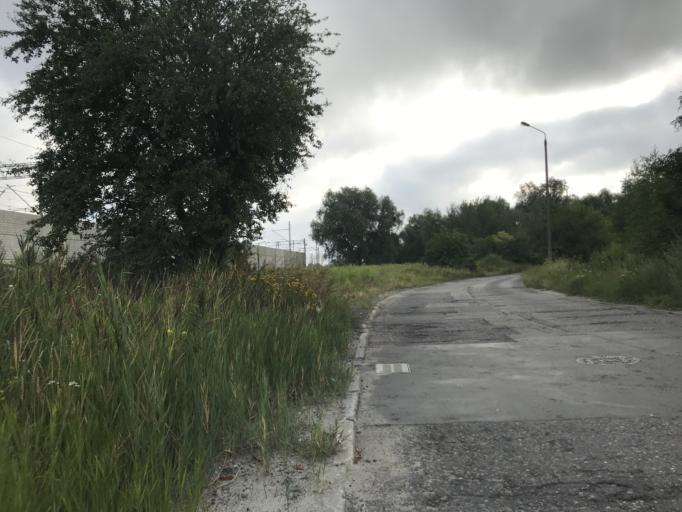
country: PL
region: Pomeranian Voivodeship
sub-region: Gdansk
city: Gdansk
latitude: 54.3382
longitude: 18.6817
